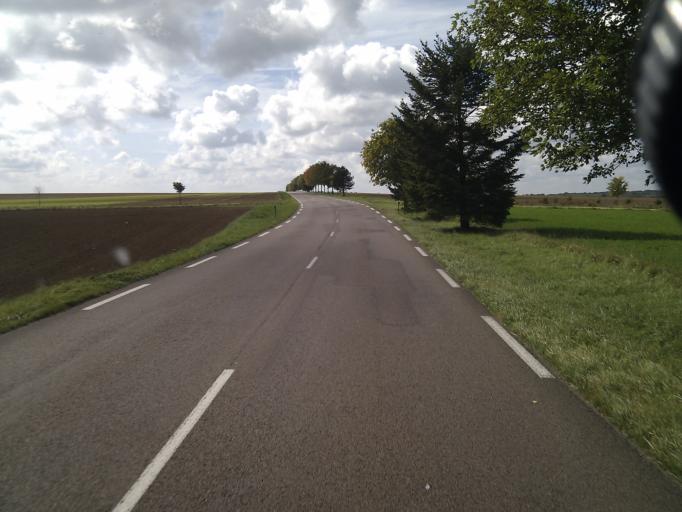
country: FR
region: Bourgogne
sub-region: Departement de la Cote-d'Or
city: Montbard
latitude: 47.7037
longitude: 4.4307
